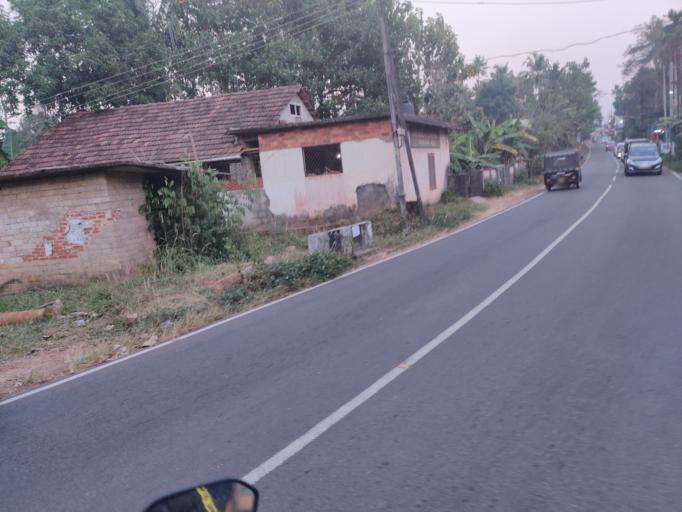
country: IN
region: Kerala
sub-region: Thrissur District
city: Kodungallur
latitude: 10.2330
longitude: 76.2805
